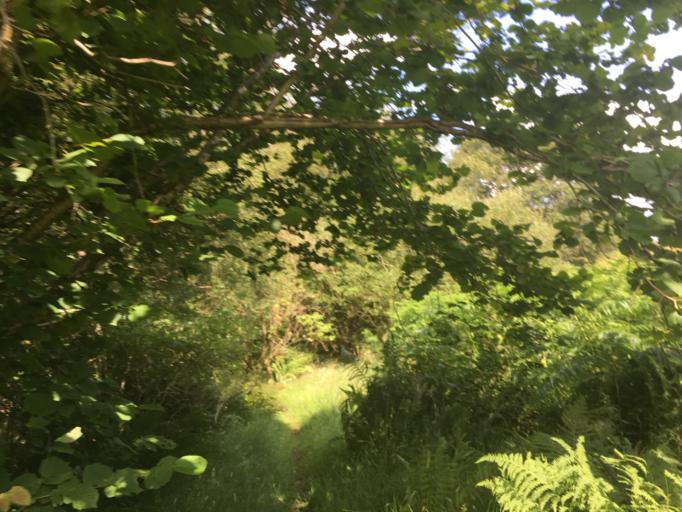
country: GB
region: Scotland
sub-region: Stirling
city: Stirling
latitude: 56.1042
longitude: -3.9831
